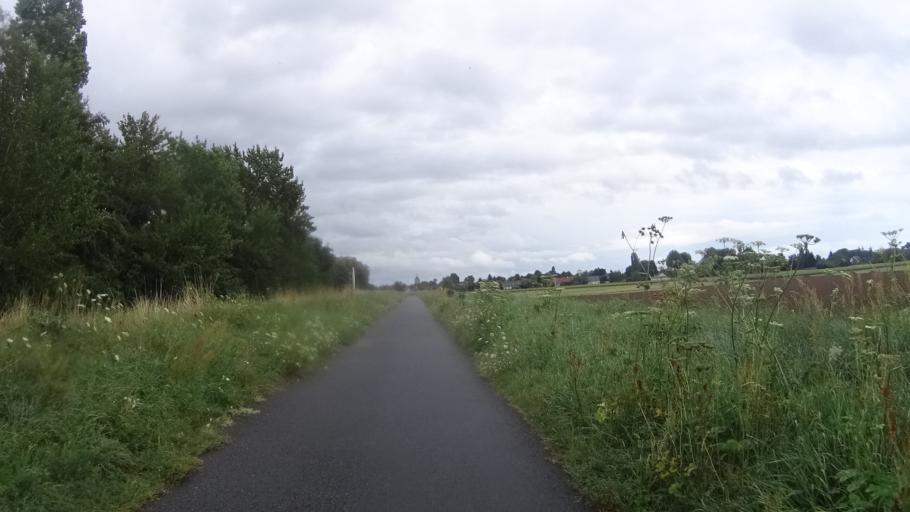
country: FR
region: Centre
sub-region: Departement du Loiret
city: Darvoy
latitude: 47.8688
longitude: 2.1046
